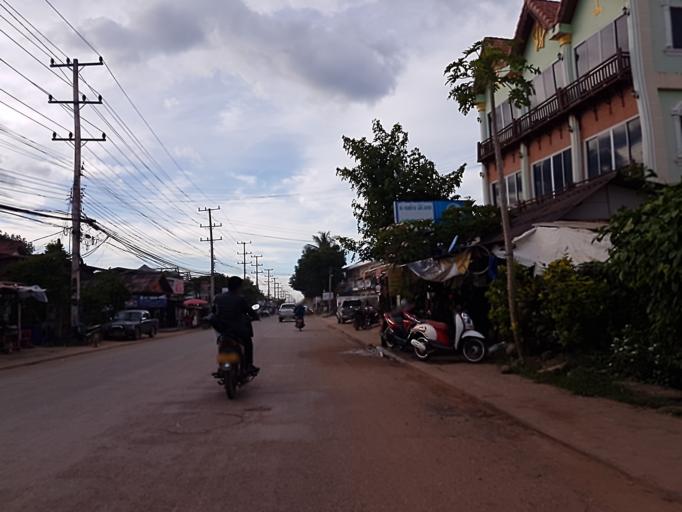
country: LA
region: Vientiane
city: Vientiane
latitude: 17.9831
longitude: 102.5826
